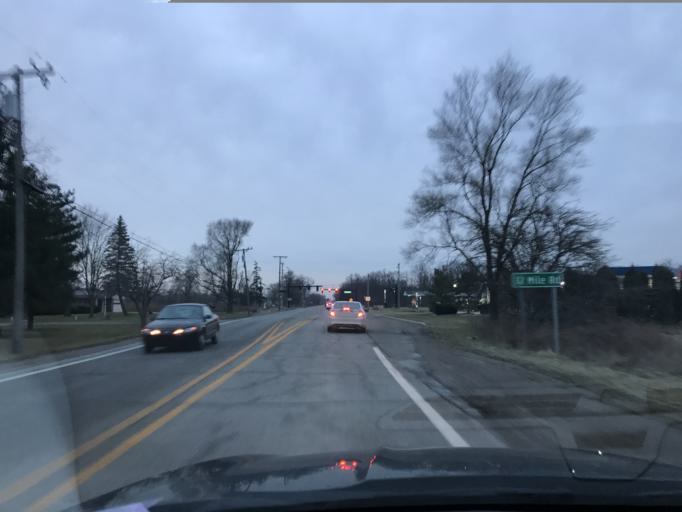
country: US
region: Michigan
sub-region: Macomb County
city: Romeo
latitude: 42.8069
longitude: -82.9626
